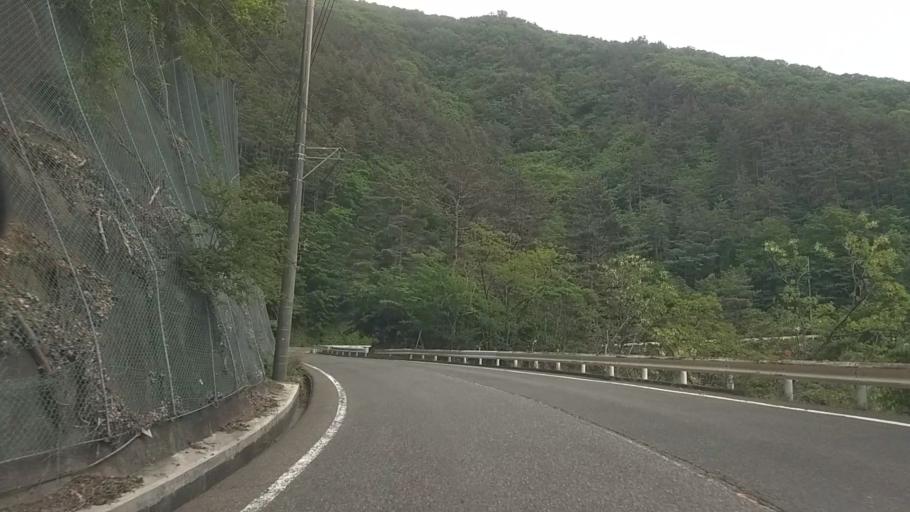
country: JP
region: Yamanashi
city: Fujikawaguchiko
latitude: 35.5187
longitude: 138.6186
